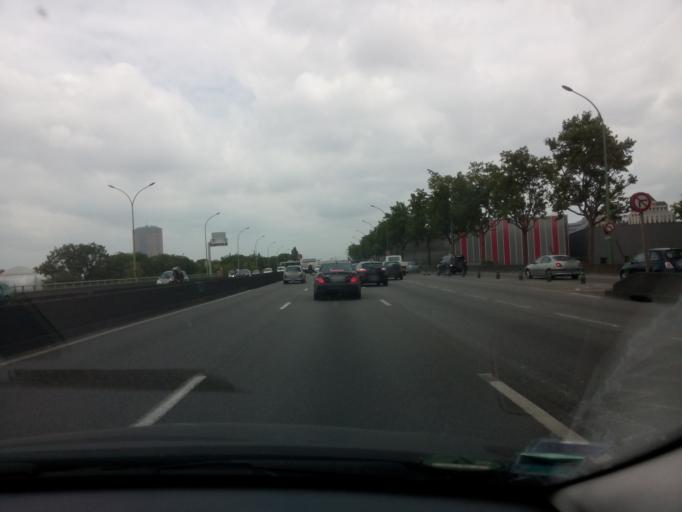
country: FR
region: Ile-de-France
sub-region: Departement de Seine-Saint-Denis
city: Le Pre-Saint-Gervais
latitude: 48.8920
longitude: 2.3957
